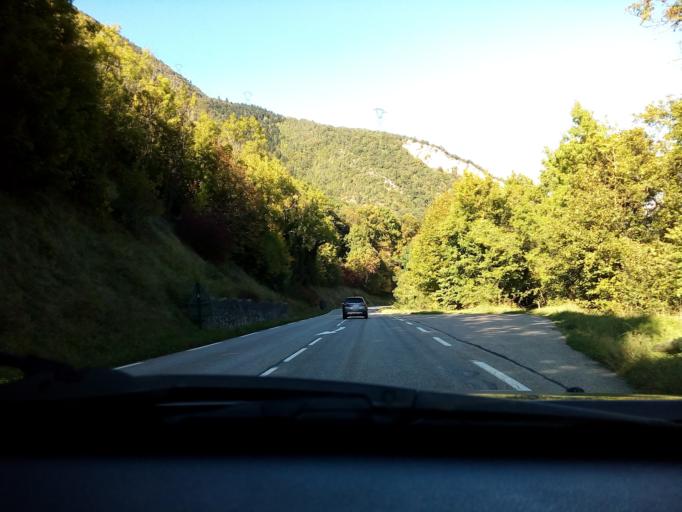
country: FR
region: Rhone-Alpes
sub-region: Departement de l'Isere
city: Sassenage
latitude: 45.2011
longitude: 5.6296
